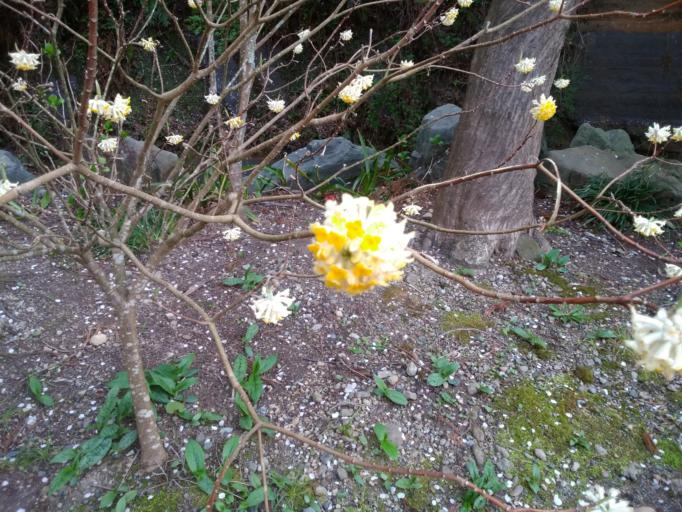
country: JP
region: Shizuoka
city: Kakegawa
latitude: 34.7345
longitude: 137.9728
